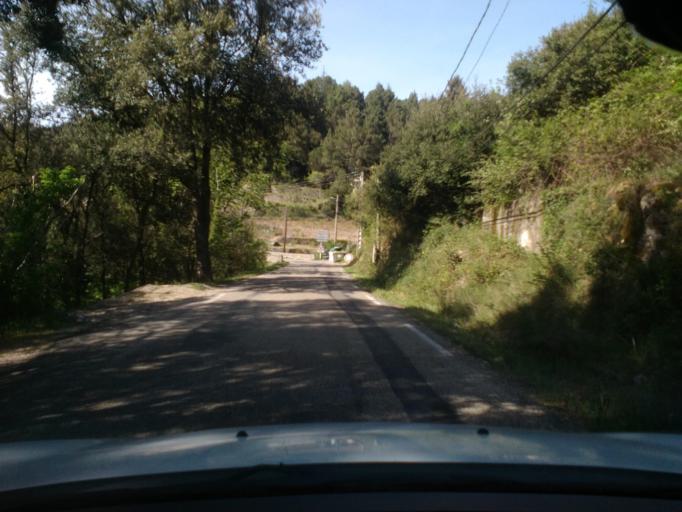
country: FR
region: Languedoc-Roussillon
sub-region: Departement du Gard
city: Lasalle
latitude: 44.0667
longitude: 3.8341
